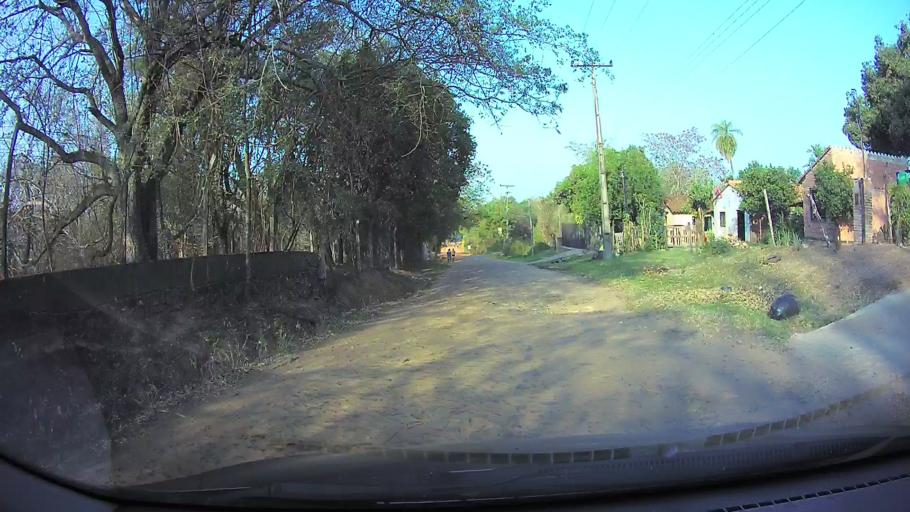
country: PY
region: Central
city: Limpio
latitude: -25.2183
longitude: -57.4972
